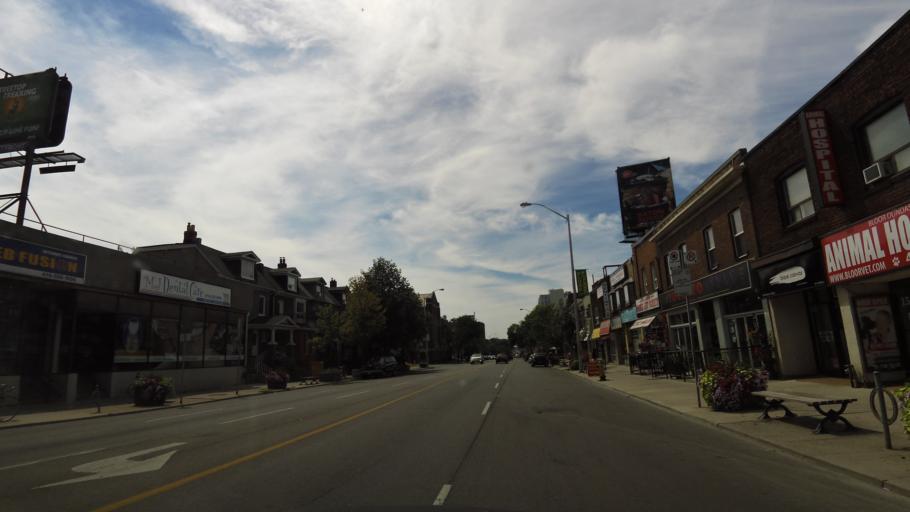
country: CA
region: Ontario
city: Toronto
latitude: 43.6563
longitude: -79.4528
